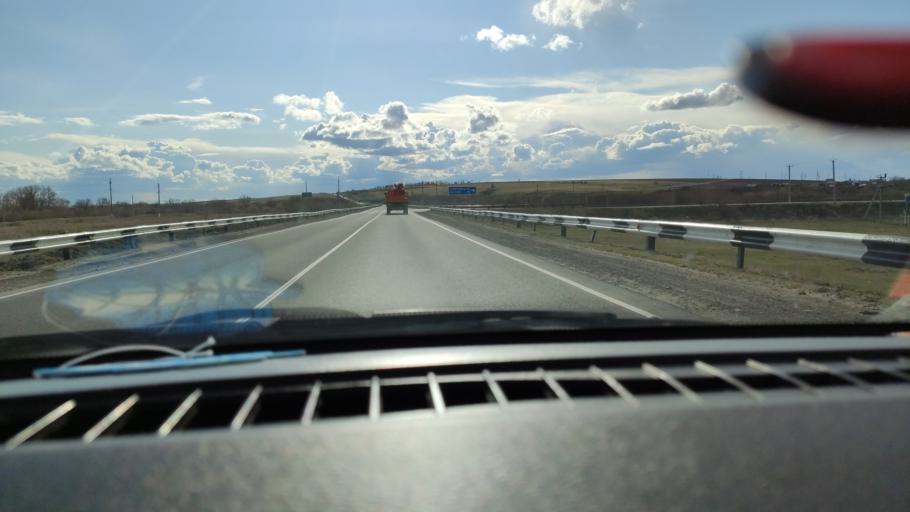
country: RU
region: Saratov
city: Sennoy
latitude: 52.1421
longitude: 46.8943
